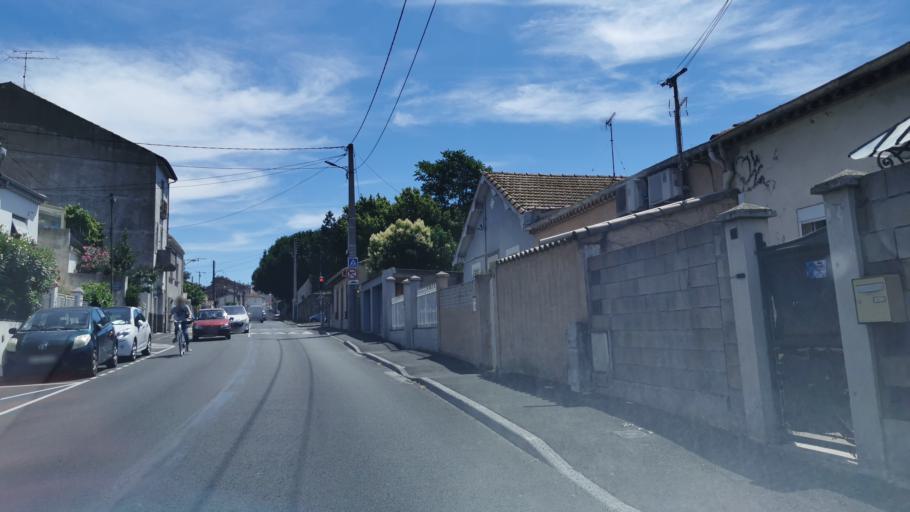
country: FR
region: Languedoc-Roussillon
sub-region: Departement de l'Herault
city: Beziers
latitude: 43.3525
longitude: 3.2146
